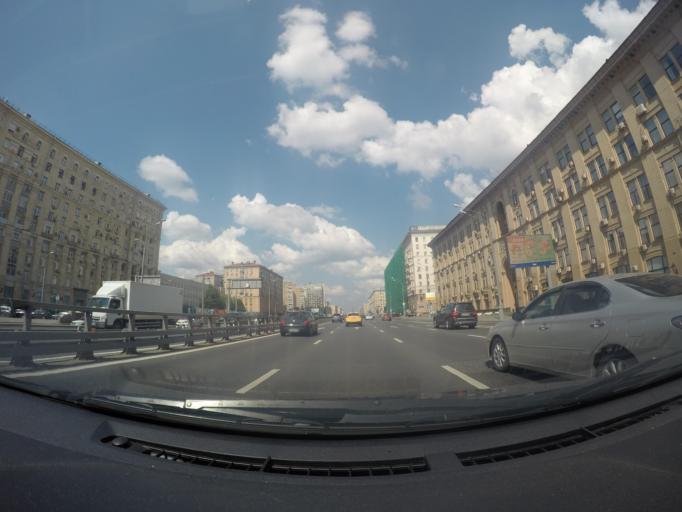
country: RU
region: Moscow
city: Mar'ina Roshcha
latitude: 55.8024
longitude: 37.6360
